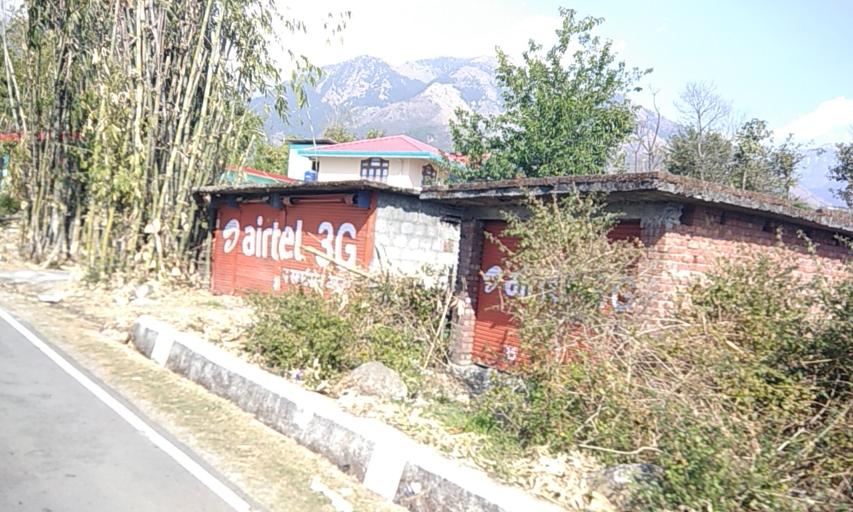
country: IN
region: Himachal Pradesh
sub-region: Kangra
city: Dharmsala
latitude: 32.1586
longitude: 76.4062
